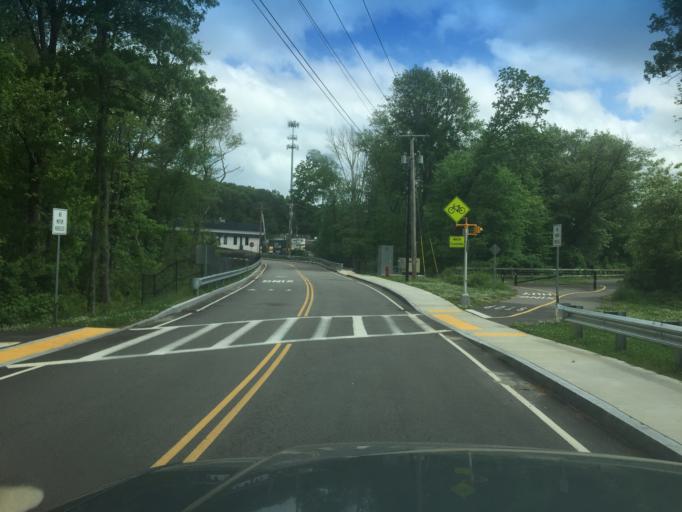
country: US
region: Massachusetts
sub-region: Worcester County
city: Milford
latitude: 42.1707
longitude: -71.5101
